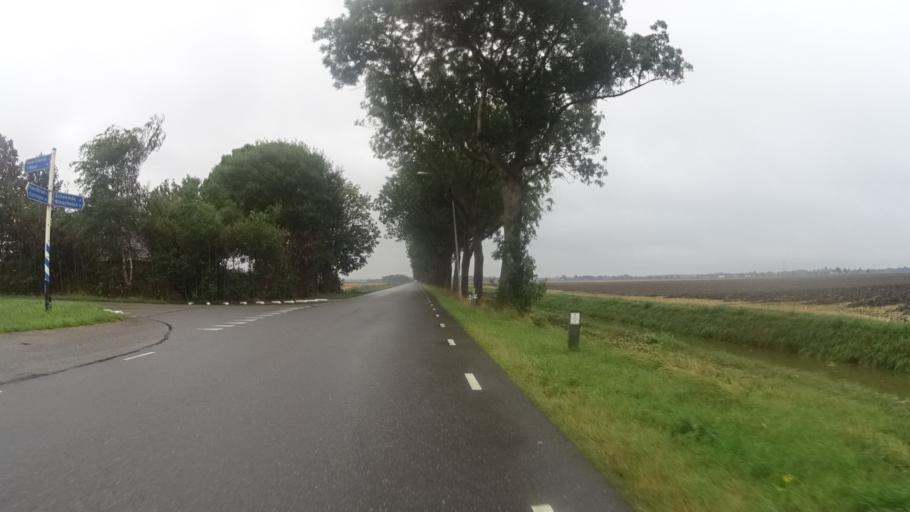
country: NL
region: Groningen
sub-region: Gemeente Veendam
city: Veendam
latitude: 53.1906
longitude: 6.9227
